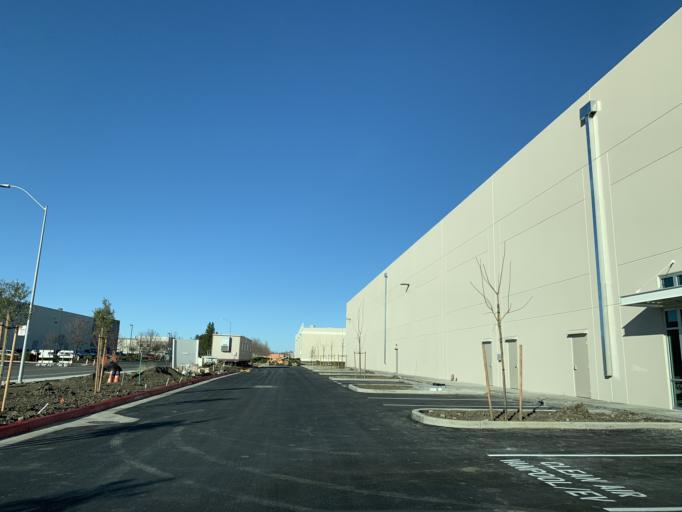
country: US
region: California
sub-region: Yolo County
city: West Sacramento
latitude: 38.5463
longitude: -121.5627
